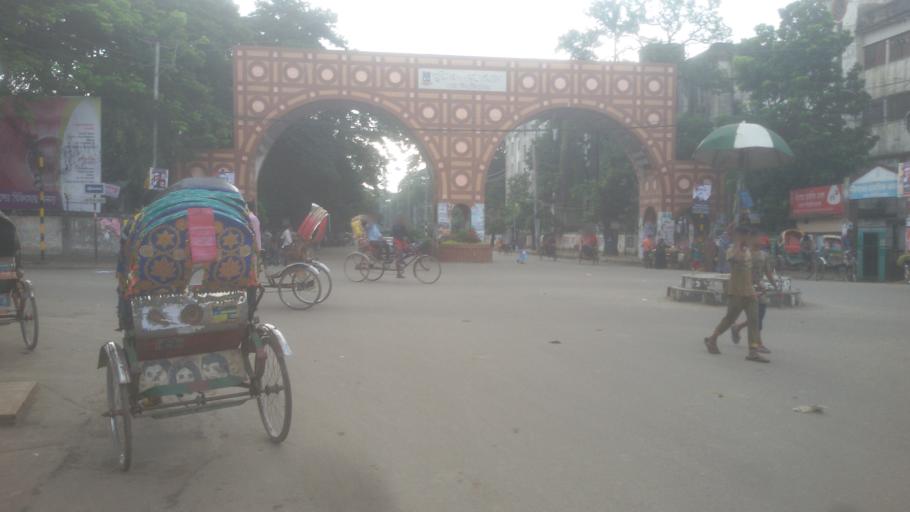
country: BD
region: Dhaka
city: Azimpur
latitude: 23.7327
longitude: 90.3869
